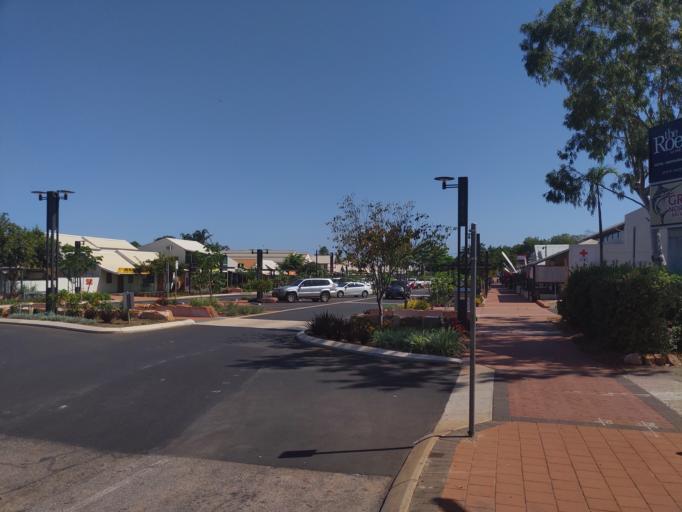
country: AU
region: Western Australia
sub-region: Broome
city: Broome
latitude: -17.9546
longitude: 122.2435
